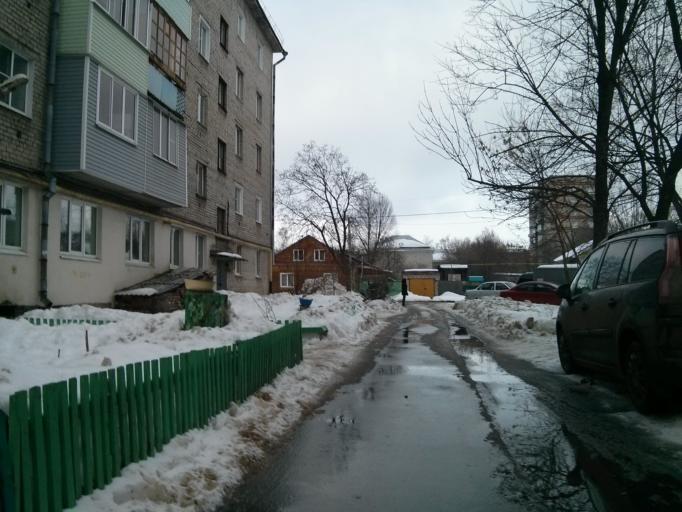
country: RU
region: Vladimir
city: Murom
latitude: 55.5661
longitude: 42.0549
